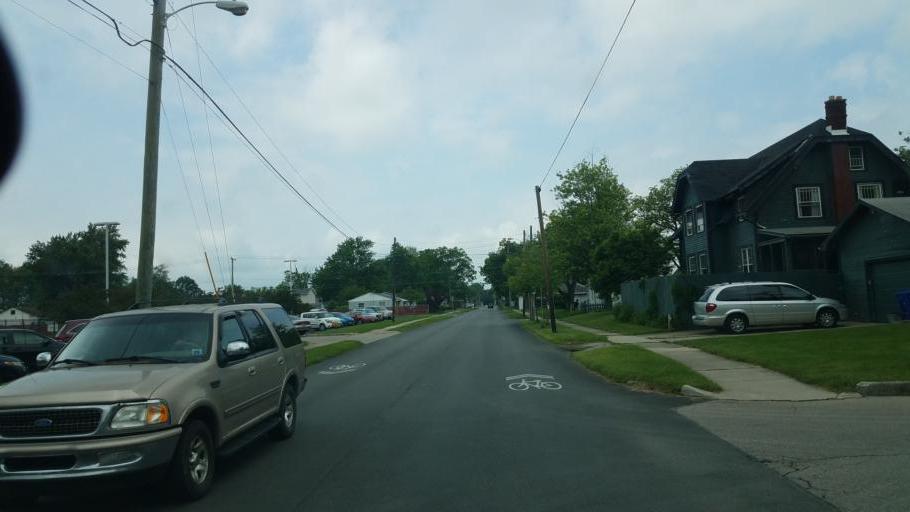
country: US
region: Ohio
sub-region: Delaware County
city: Delaware
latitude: 40.2959
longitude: -83.0786
